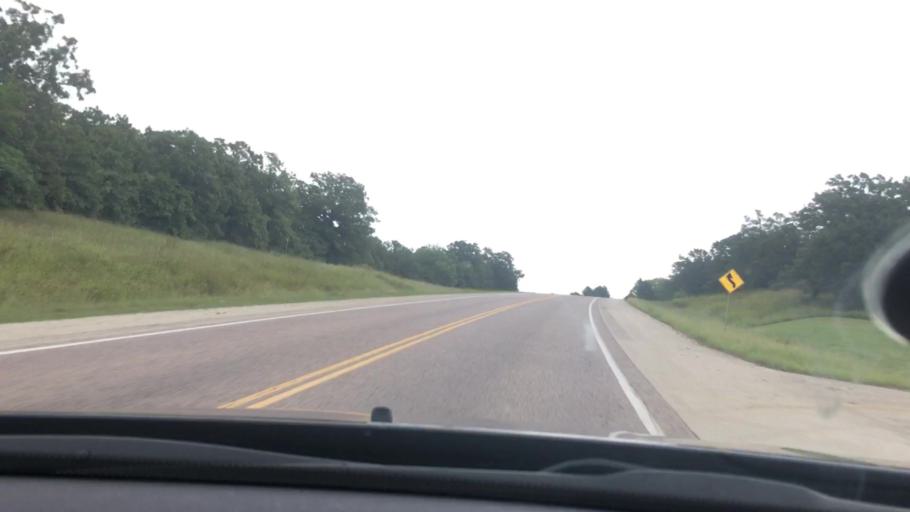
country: US
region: Oklahoma
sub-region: Pontotoc County
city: Ada
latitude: 34.7818
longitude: -96.5791
